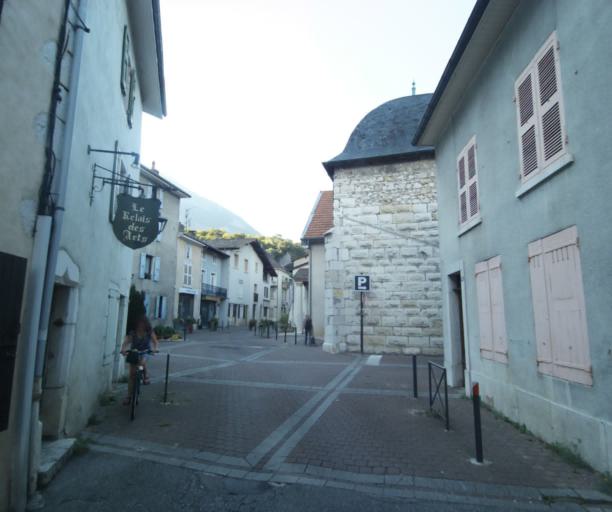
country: FR
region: Rhone-Alpes
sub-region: Departement de l'Isere
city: Sassenage
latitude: 45.2071
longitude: 5.6588
